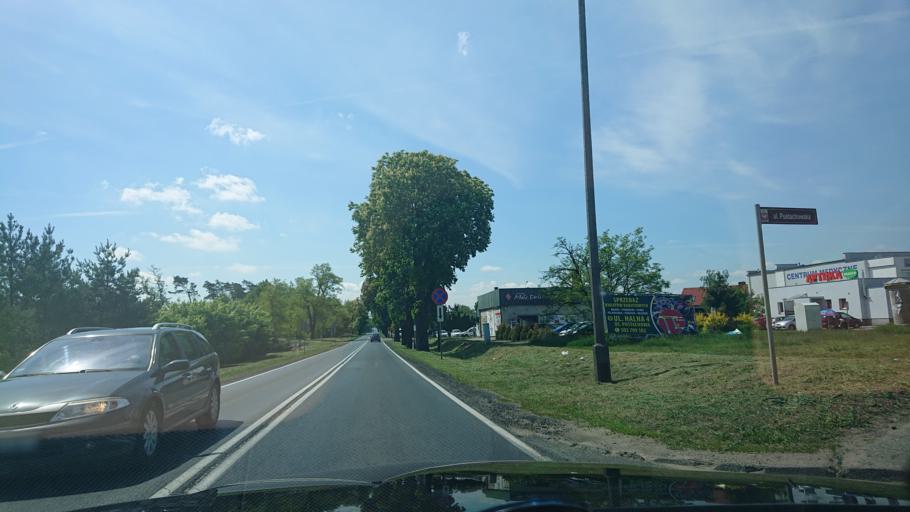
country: PL
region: Greater Poland Voivodeship
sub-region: Powiat gnieznienski
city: Gniezno
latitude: 52.5077
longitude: 17.5948
